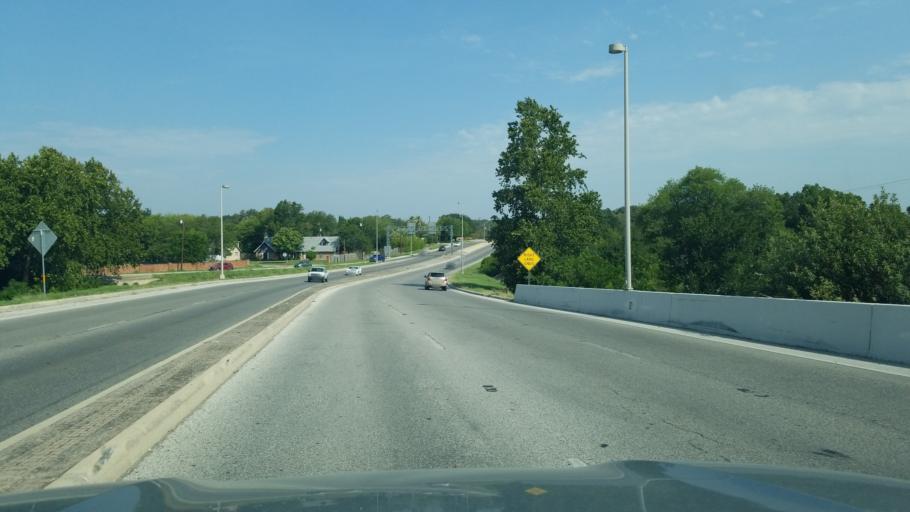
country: US
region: Texas
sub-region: Bexar County
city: Castle Hills
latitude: 29.5217
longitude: -98.5137
